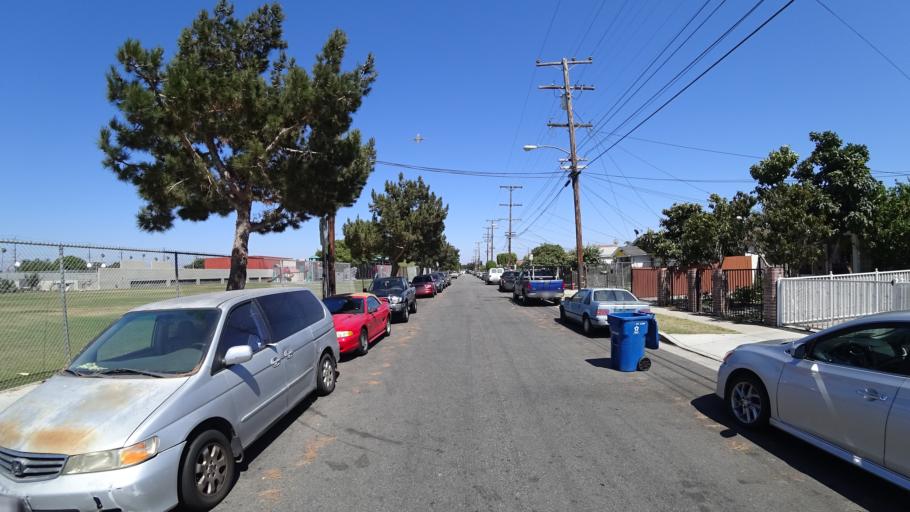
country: US
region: California
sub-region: Los Angeles County
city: Lennox
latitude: 33.9409
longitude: -118.3477
